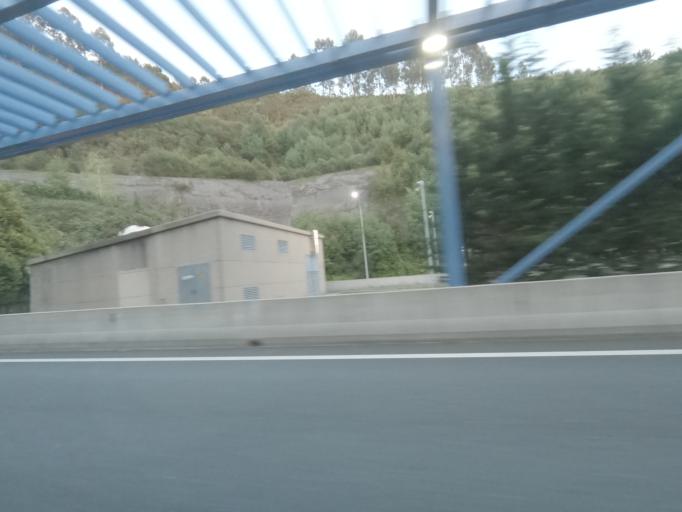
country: ES
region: Galicia
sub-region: Provincia de Pontevedra
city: Covelo
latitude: 42.1749
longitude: -8.3695
